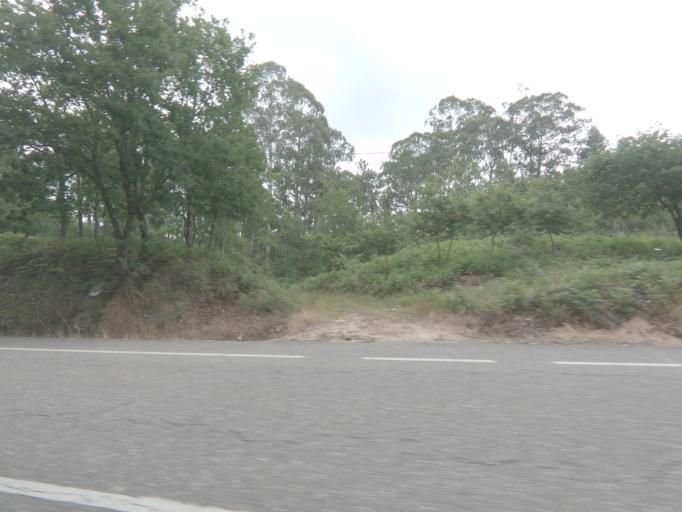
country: ES
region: Galicia
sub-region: Provincia de Pontevedra
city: O Rosal
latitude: 41.9349
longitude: -8.7929
